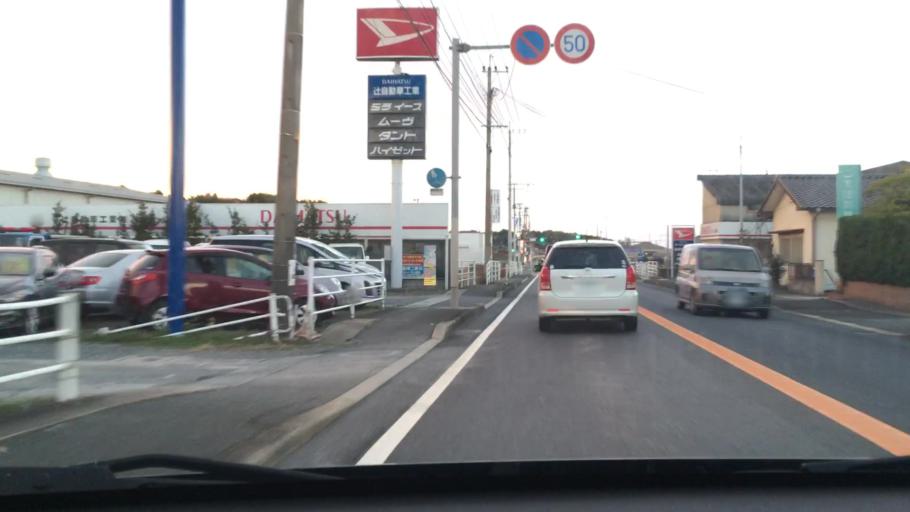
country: JP
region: Fukuoka
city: Shiida
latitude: 33.6325
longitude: 131.0804
